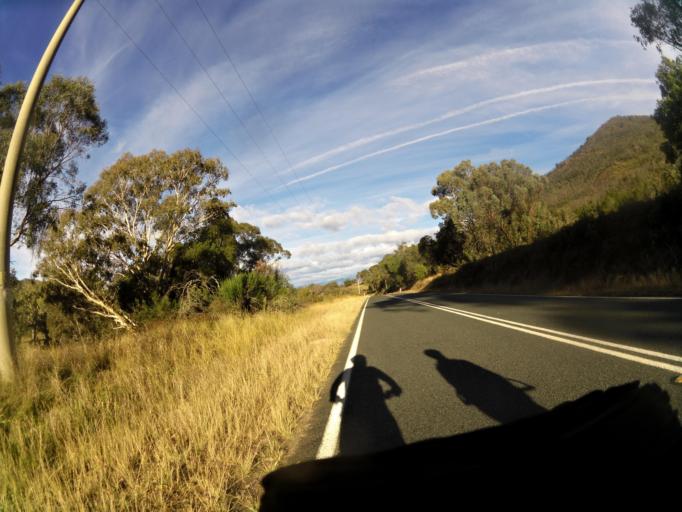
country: AU
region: New South Wales
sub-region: Greater Hume Shire
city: Holbrook
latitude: -35.9924
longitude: 147.8578
